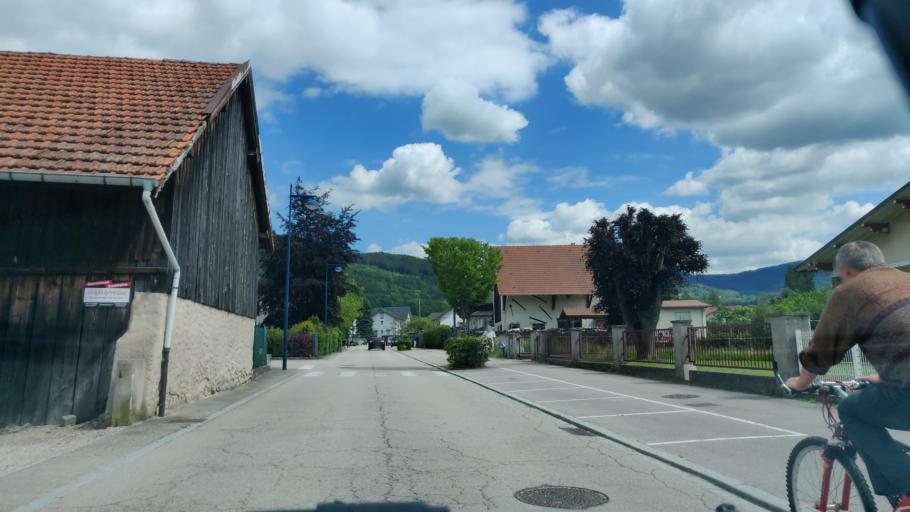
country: FR
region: Lorraine
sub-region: Departement des Vosges
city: Fraize
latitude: 48.1849
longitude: 7.0057
